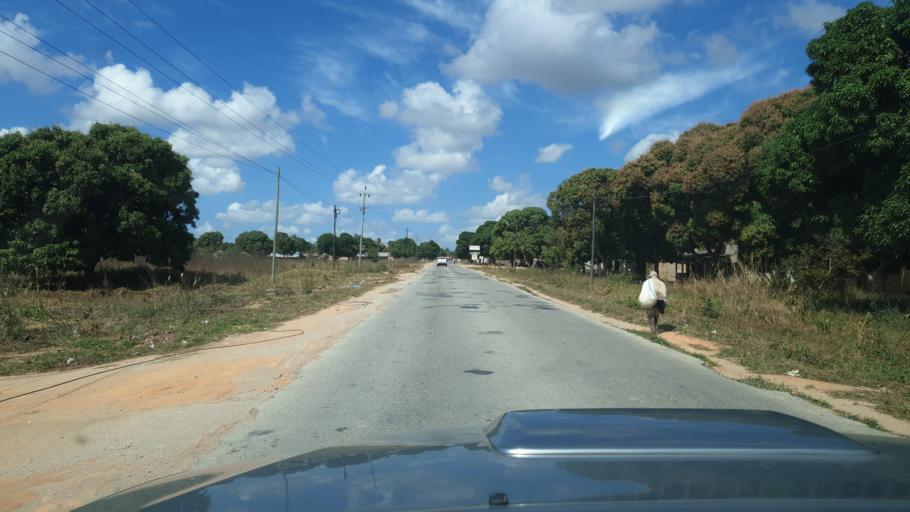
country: MZ
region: Nampula
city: Nacala
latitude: -14.5040
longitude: 40.6974
